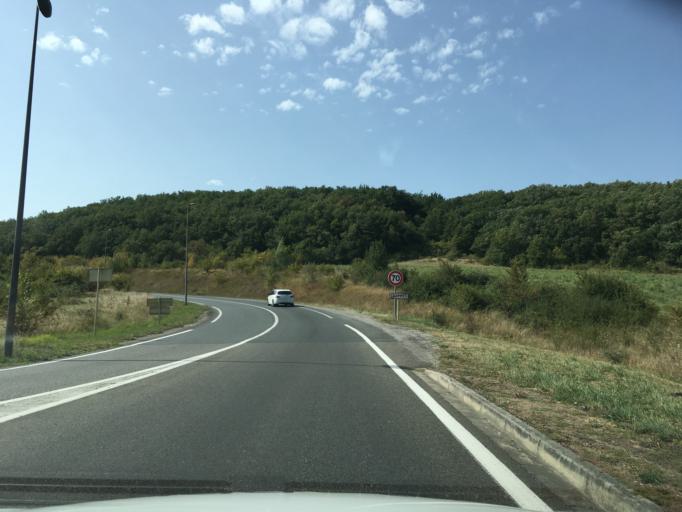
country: FR
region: Midi-Pyrenees
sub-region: Departement du Tarn
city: Lagarrigue
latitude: 43.5874
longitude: 2.2705
